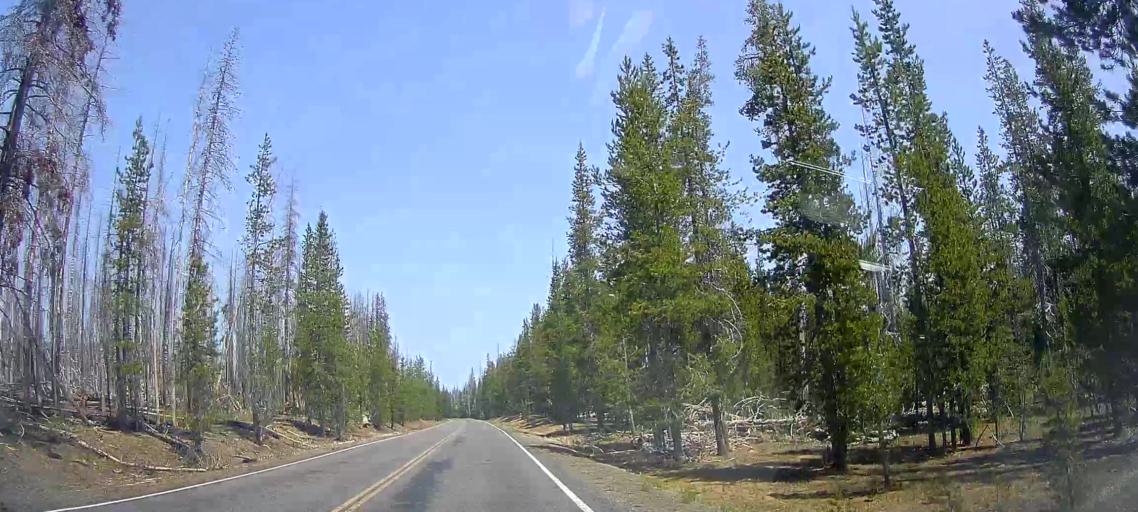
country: US
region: Oregon
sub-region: Lane County
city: Oakridge
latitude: 43.0401
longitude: -122.1173
